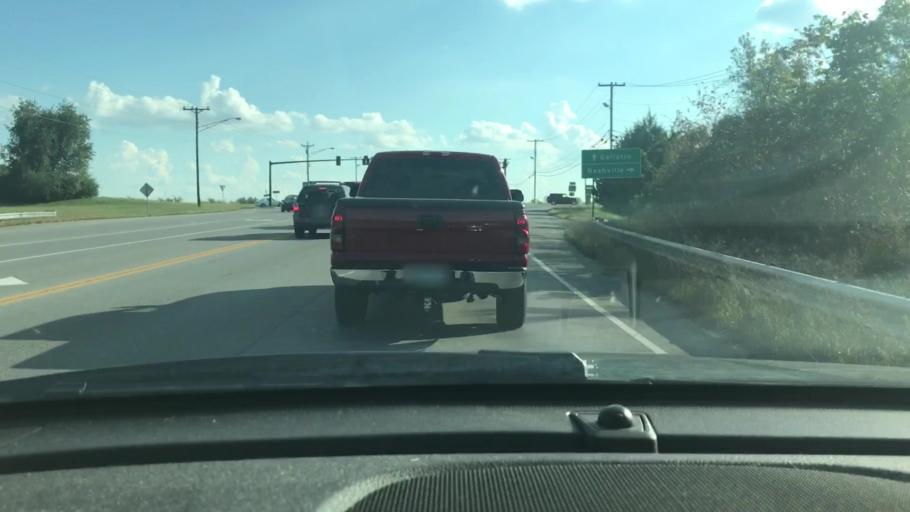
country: US
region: Tennessee
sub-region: Sumner County
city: Hendersonville
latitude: 36.3327
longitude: -86.6184
